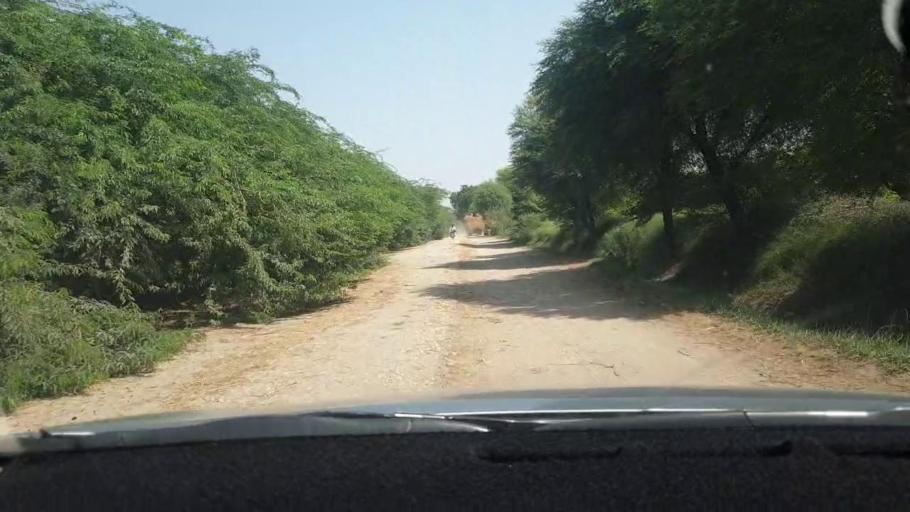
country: PK
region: Sindh
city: Tando Mittha Khan
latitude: 25.8451
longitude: 69.4499
